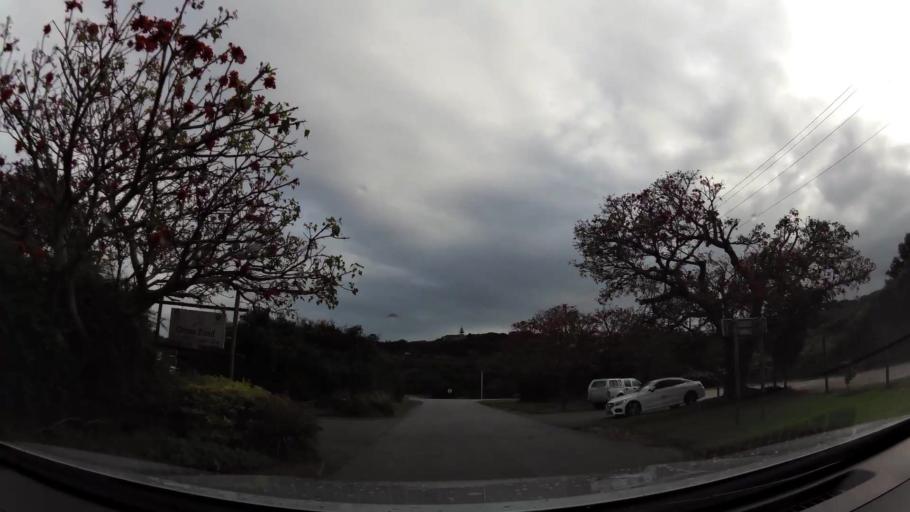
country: ZA
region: Eastern Cape
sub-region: Nelson Mandela Bay Metropolitan Municipality
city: Port Elizabeth
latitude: -34.0115
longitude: 25.4964
